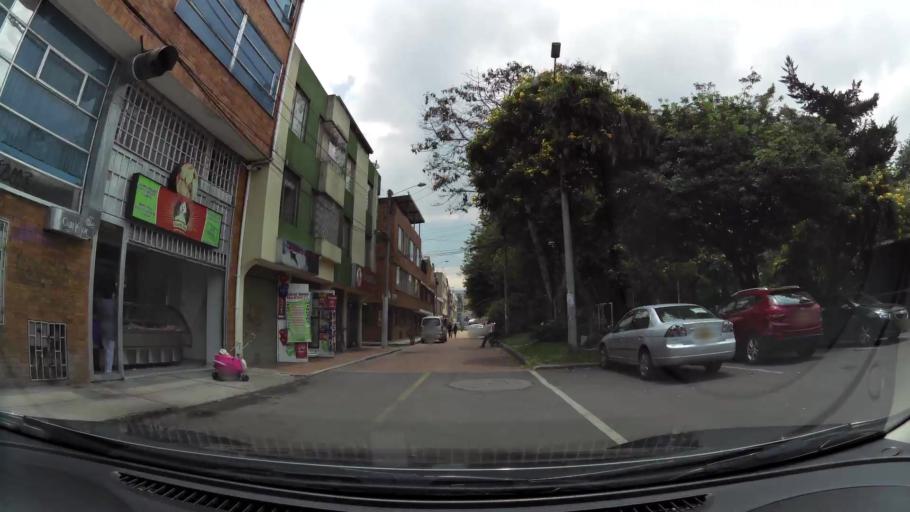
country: CO
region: Cundinamarca
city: Cota
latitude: 4.7461
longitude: -74.0628
